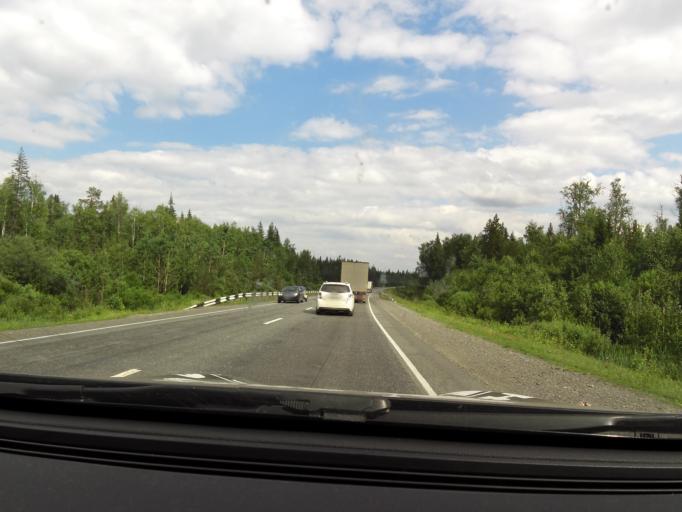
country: RU
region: Sverdlovsk
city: Atig
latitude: 56.8223
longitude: 59.3326
